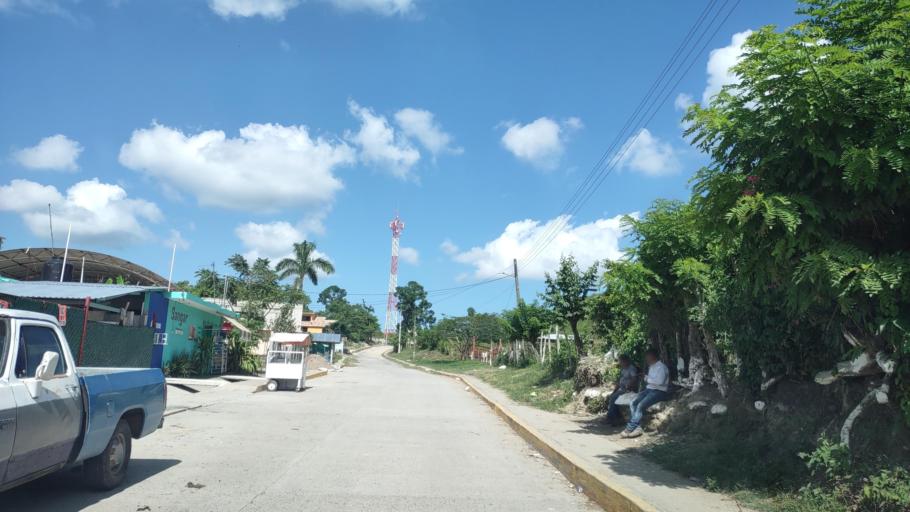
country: MM
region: Shan
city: Taunggyi
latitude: 20.5862
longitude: 97.3736
